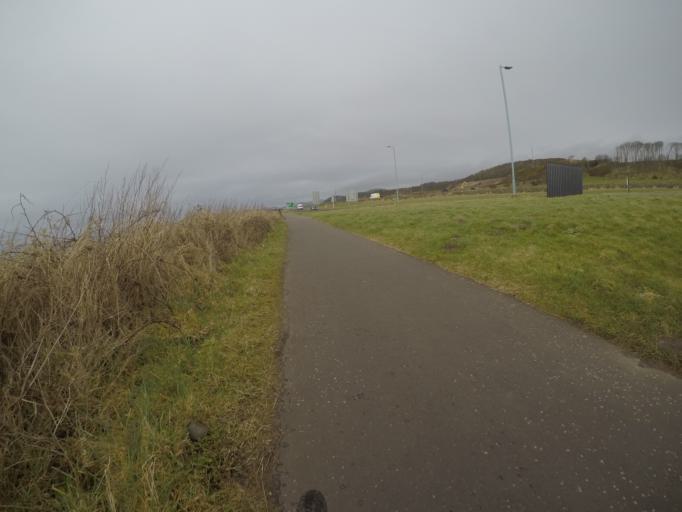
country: GB
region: Scotland
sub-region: North Ayrshire
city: Ardrossan
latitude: 55.6551
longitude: -4.8258
